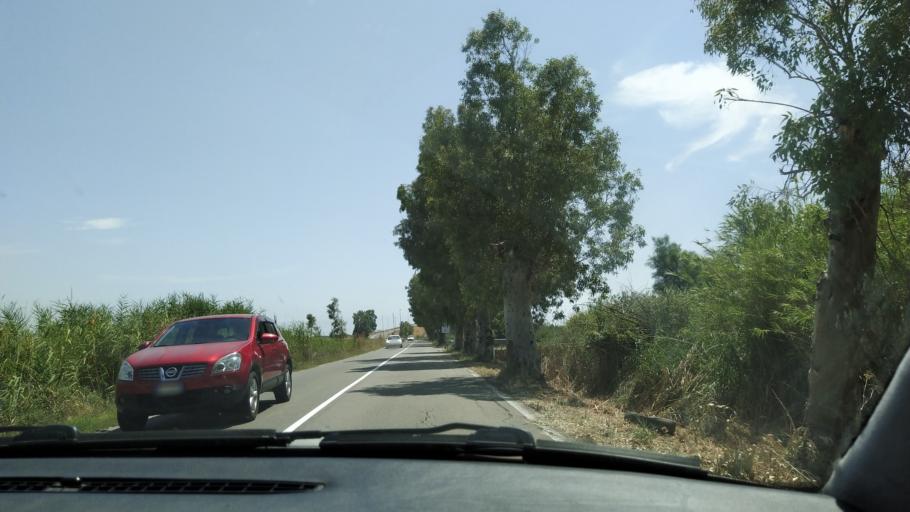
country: IT
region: Basilicate
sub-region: Provincia di Matera
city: Marconia
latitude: 40.3374
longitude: 16.7701
